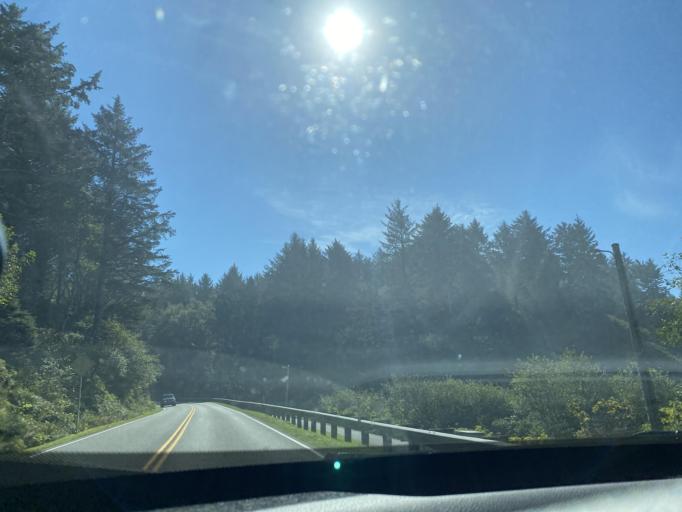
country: US
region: Washington
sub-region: Clallam County
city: Forks
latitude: 47.8999
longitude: -124.6262
